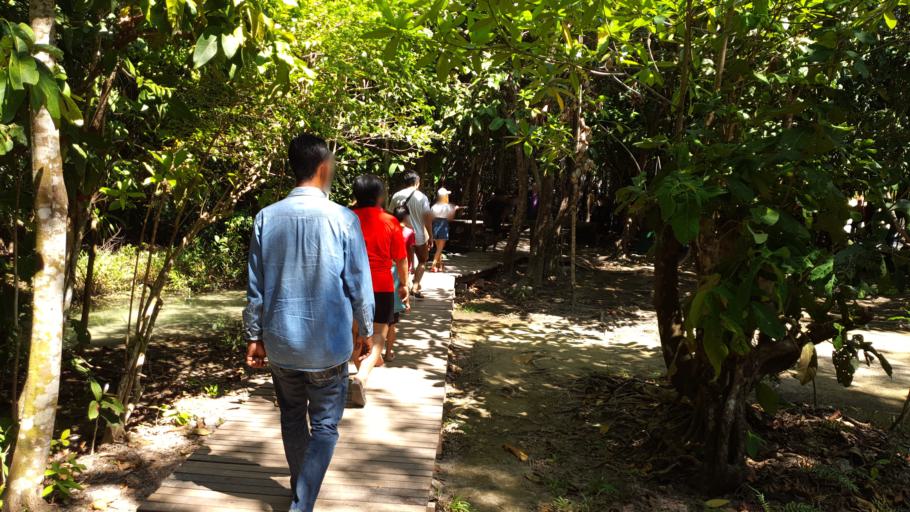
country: TH
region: Krabi
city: Khlong Thom
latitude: 7.9252
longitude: 99.2677
